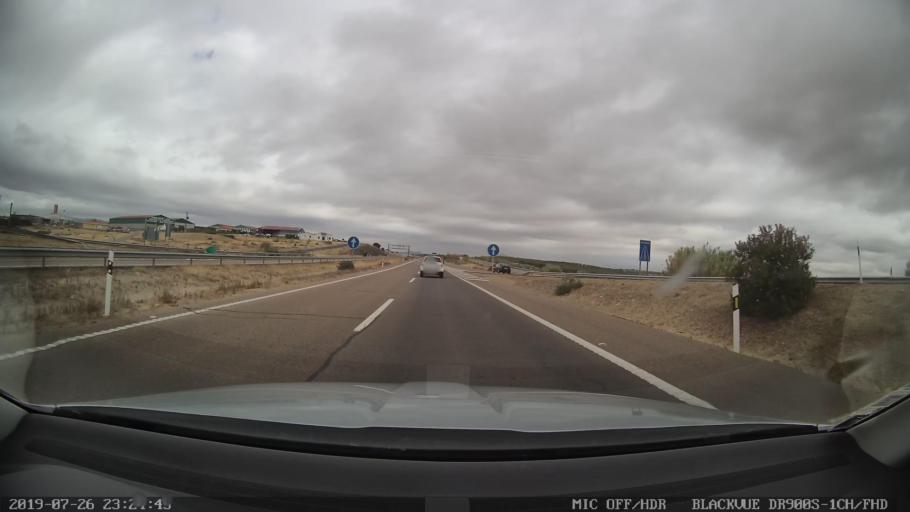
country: ES
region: Extremadura
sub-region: Provincia de Caceres
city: Escurial
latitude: 39.1766
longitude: -5.8969
